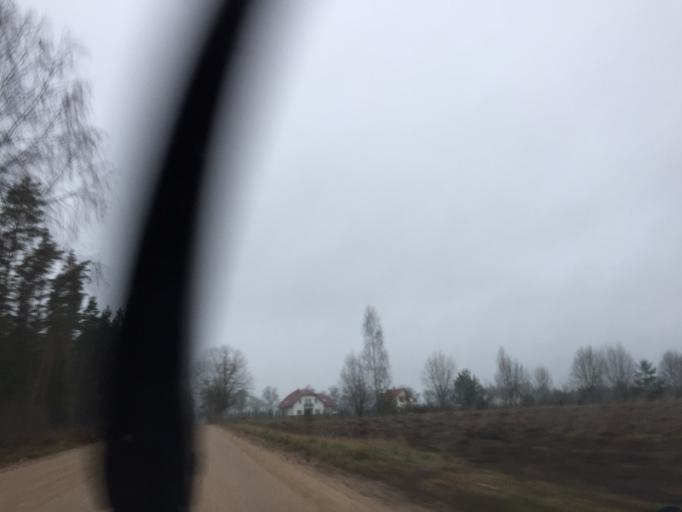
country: LV
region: Koceni
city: Koceni
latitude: 57.5368
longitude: 25.3336
